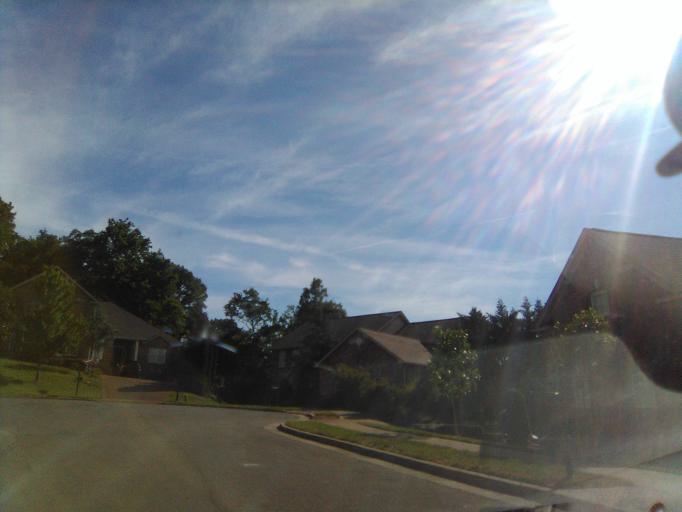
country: US
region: Tennessee
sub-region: Davidson County
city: Belle Meade
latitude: 36.1145
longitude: -86.9119
